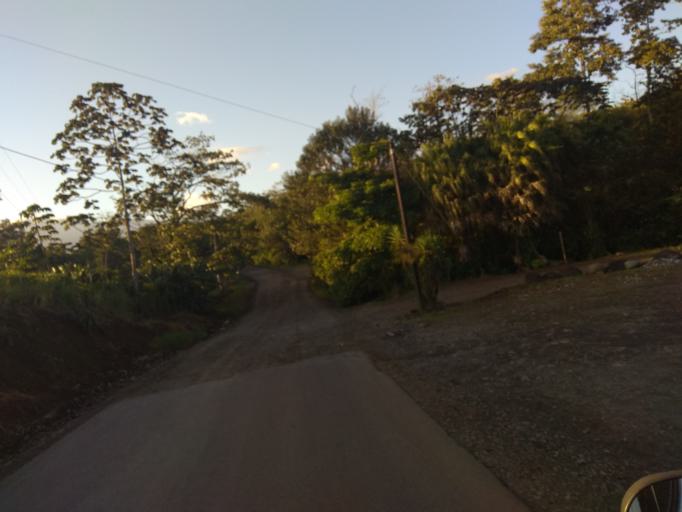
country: CR
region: Alajuela
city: Pital
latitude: 10.3791
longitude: -84.2646
